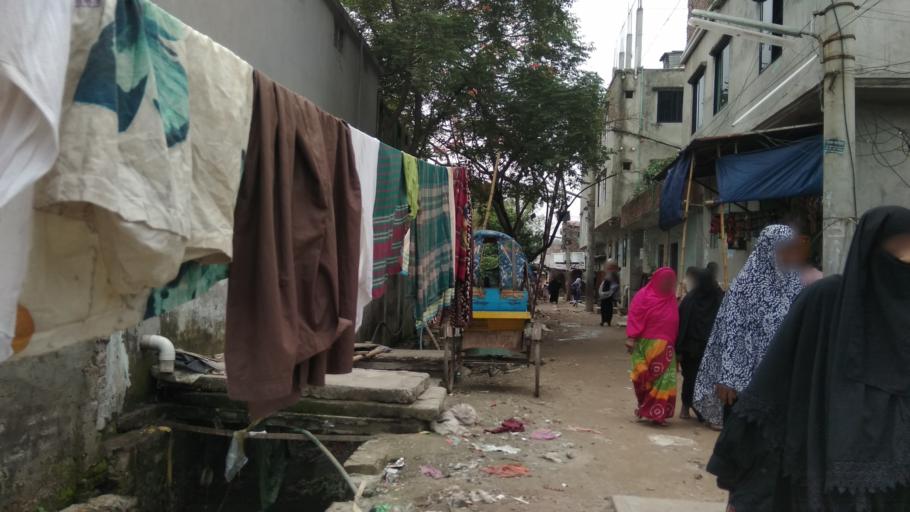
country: BD
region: Dhaka
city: Tungi
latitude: 23.8174
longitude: 90.3822
